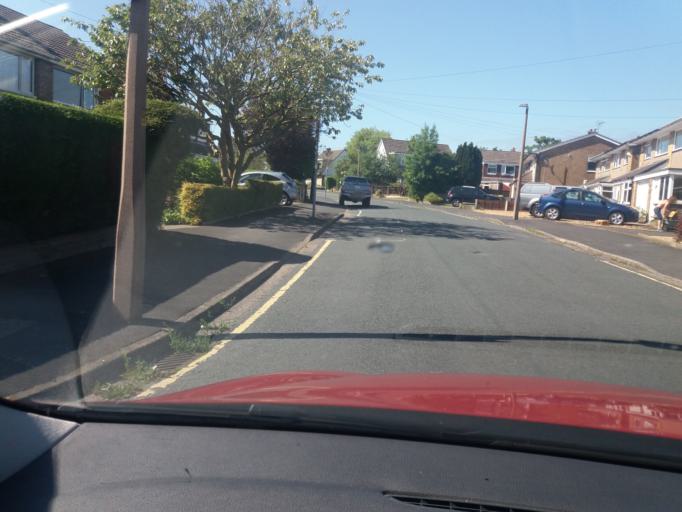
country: GB
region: England
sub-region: Lancashire
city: Preston
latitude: 53.7950
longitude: -2.7051
